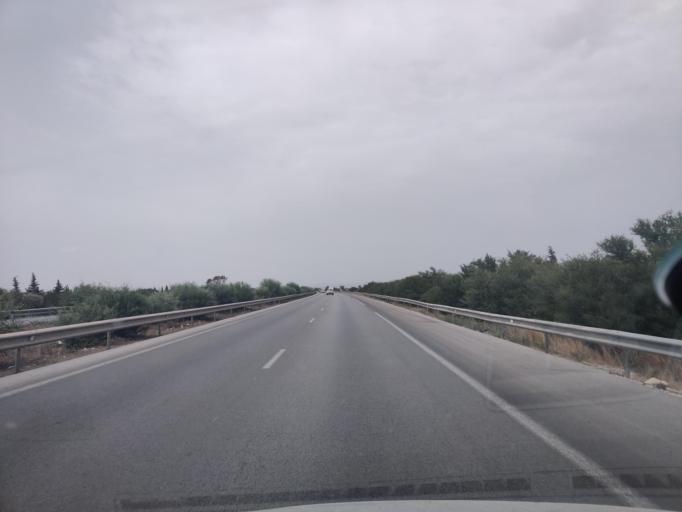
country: TN
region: Susah
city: Harqalah
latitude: 36.0292
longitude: 10.4251
